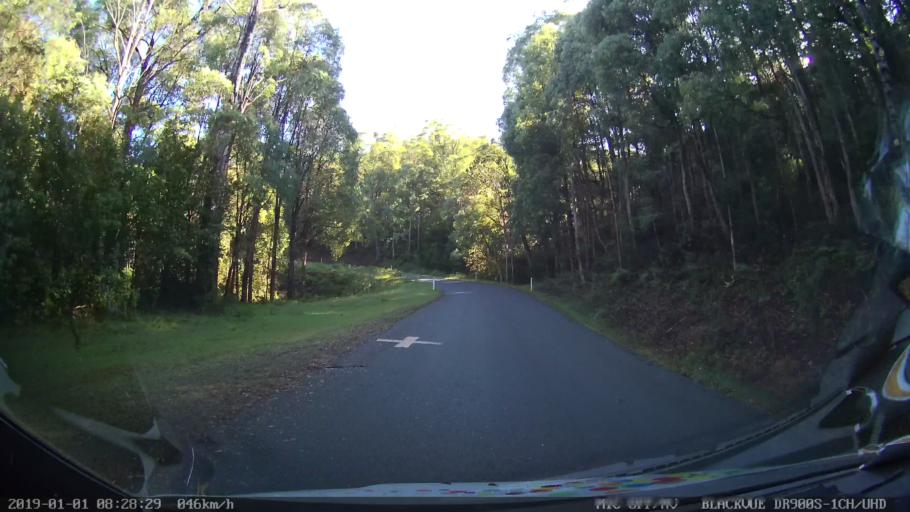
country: AU
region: New South Wales
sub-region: Snowy River
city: Jindabyne
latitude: -36.3763
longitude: 148.1900
